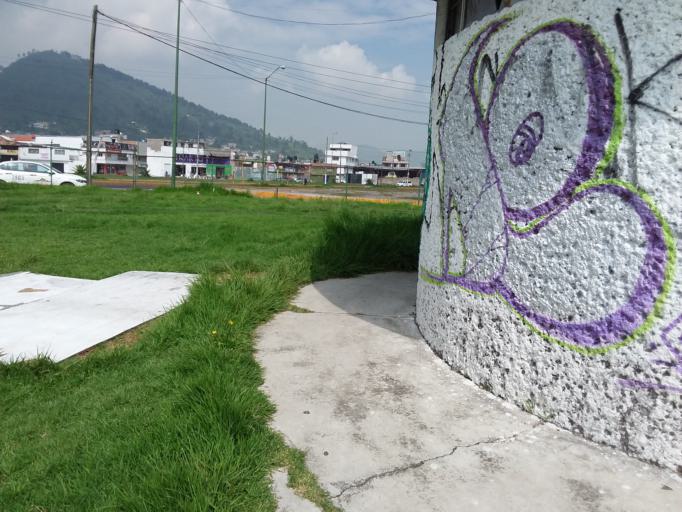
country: MX
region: Mexico
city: San Marcos Yachihuacaltepec
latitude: 19.3171
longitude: -99.6508
